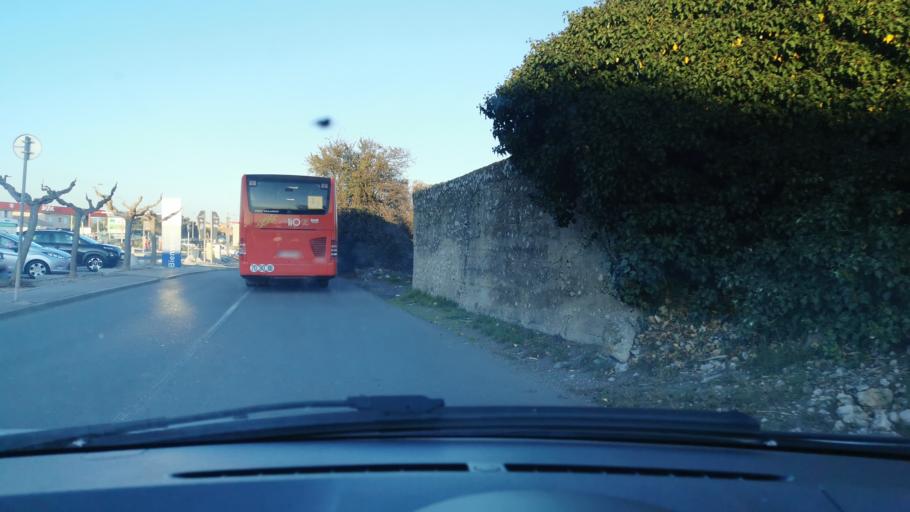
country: FR
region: Languedoc-Roussillon
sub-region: Departement de l'Herault
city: Frontignan
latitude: 43.4338
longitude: 3.7378
